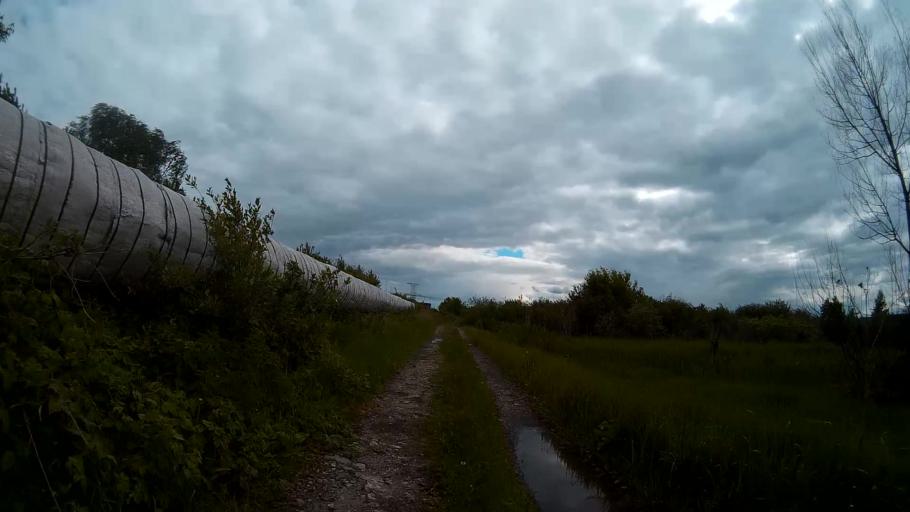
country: RU
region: Ulyanovsk
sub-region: Ulyanovskiy Rayon
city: Ulyanovsk
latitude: 54.2437
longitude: 48.2996
